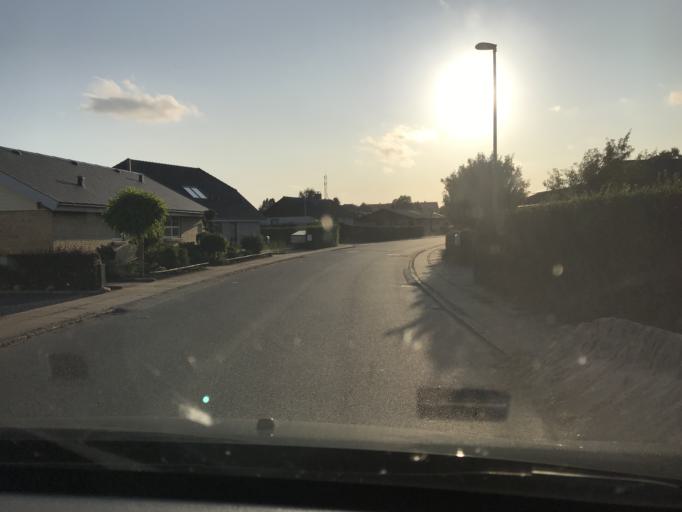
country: DK
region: South Denmark
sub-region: Vejle Kommune
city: Vejle
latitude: 55.7169
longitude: 9.5704
